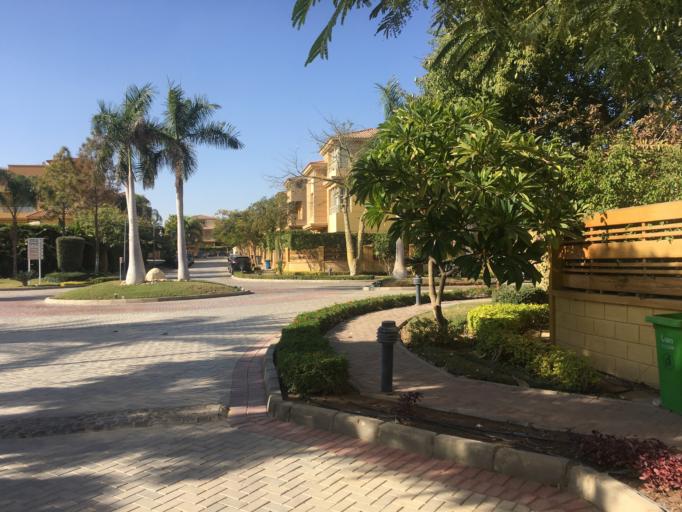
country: EG
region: Al Jizah
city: Awsim
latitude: 30.0592
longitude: 30.9873
